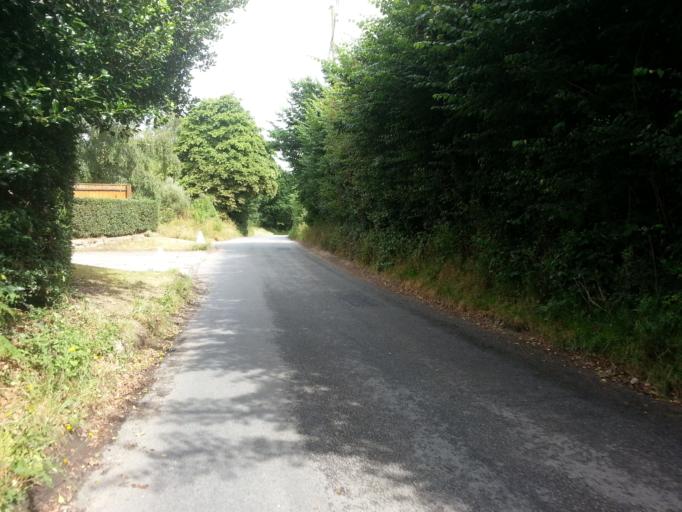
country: GB
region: England
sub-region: Suffolk
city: Ipswich
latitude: 51.9825
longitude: 1.1589
